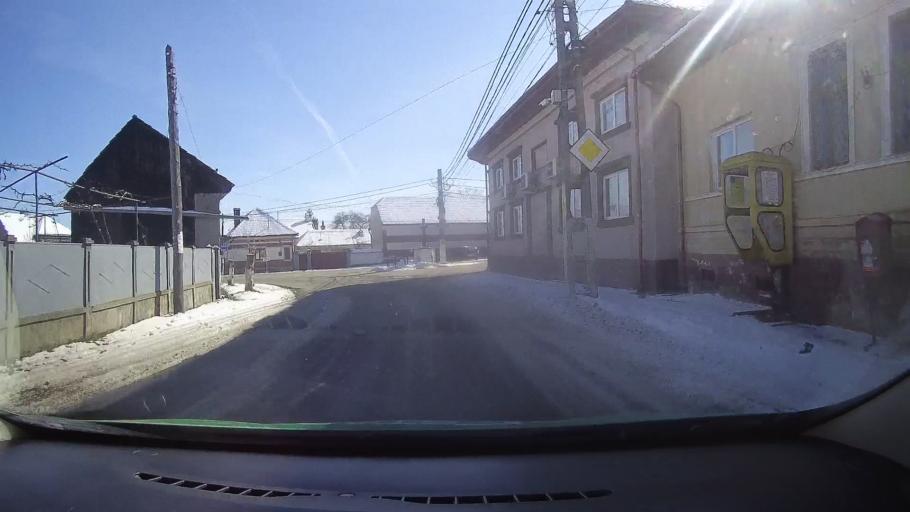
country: RO
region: Brasov
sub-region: Comuna Recea
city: Recea
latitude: 45.7319
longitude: 24.9435
